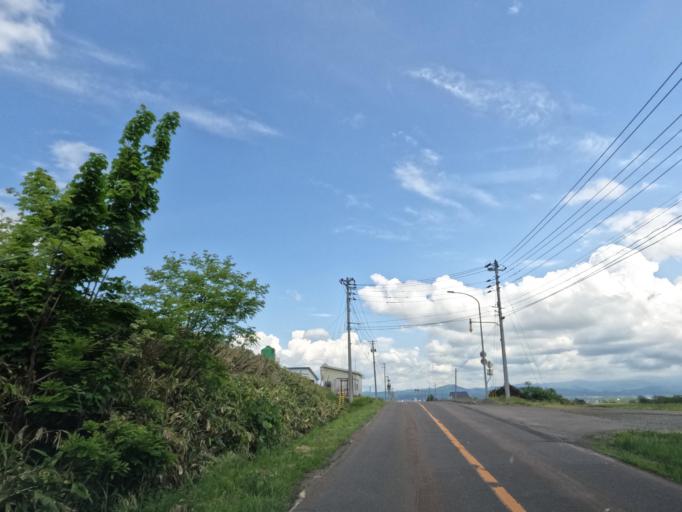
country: JP
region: Hokkaido
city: Takikawa
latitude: 43.5781
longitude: 141.8410
